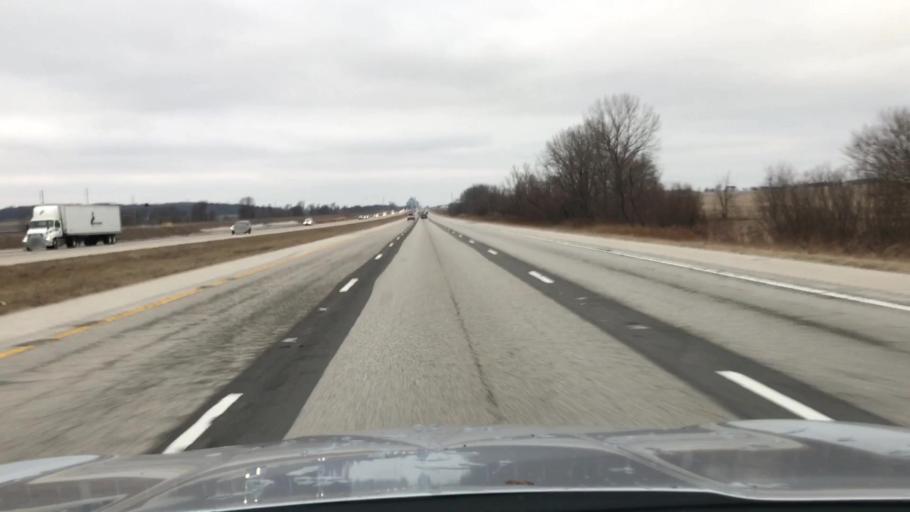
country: US
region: Illinois
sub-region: Sangamon County
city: Williamsville
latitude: 40.0484
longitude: -89.4608
